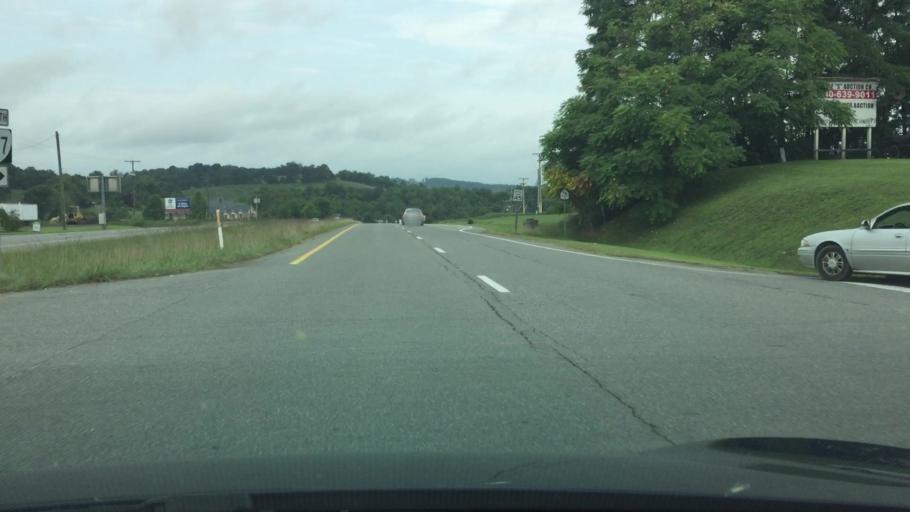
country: US
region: Virginia
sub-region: City of Radford
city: Radford
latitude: 37.1006
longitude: -80.5130
